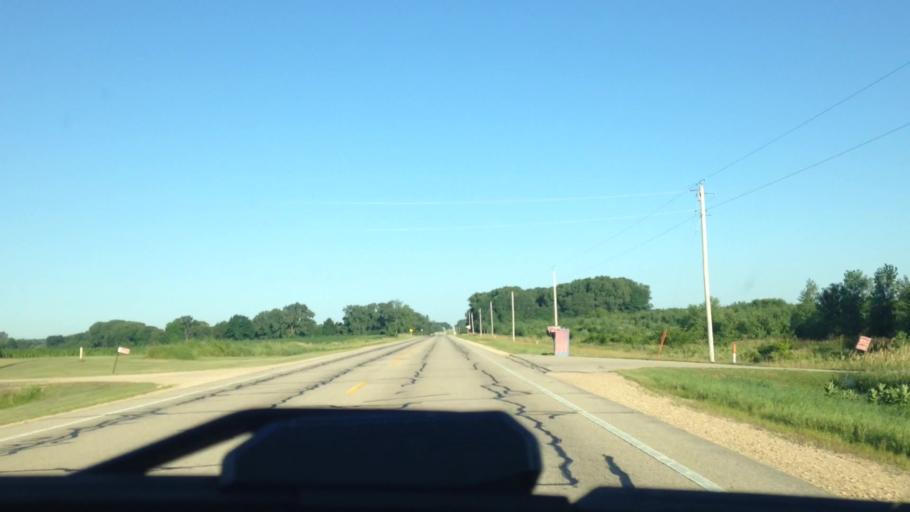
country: US
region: Wisconsin
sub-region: Columbia County
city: Fall River
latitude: 43.3408
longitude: -89.1184
